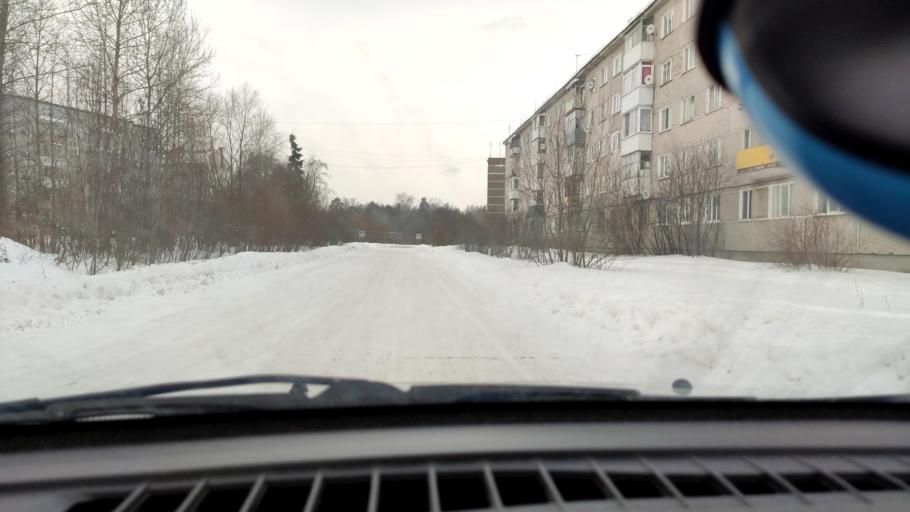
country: RU
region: Perm
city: Overyata
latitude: 58.0755
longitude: 55.8713
